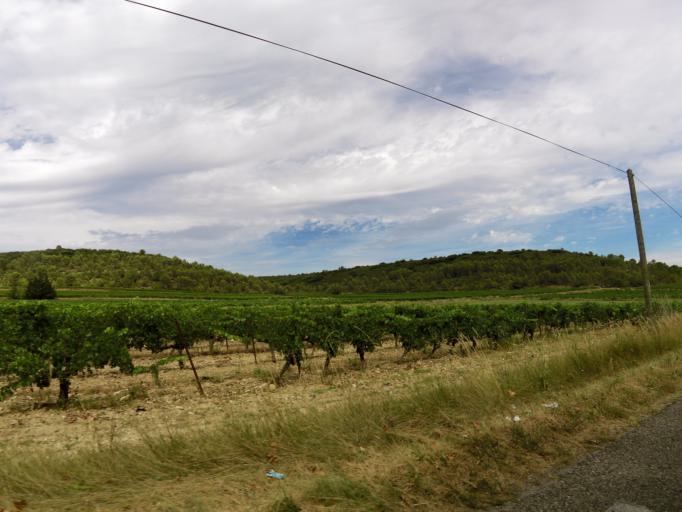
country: FR
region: Languedoc-Roussillon
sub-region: Departement du Gard
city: Congenies
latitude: 43.8008
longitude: 4.1588
